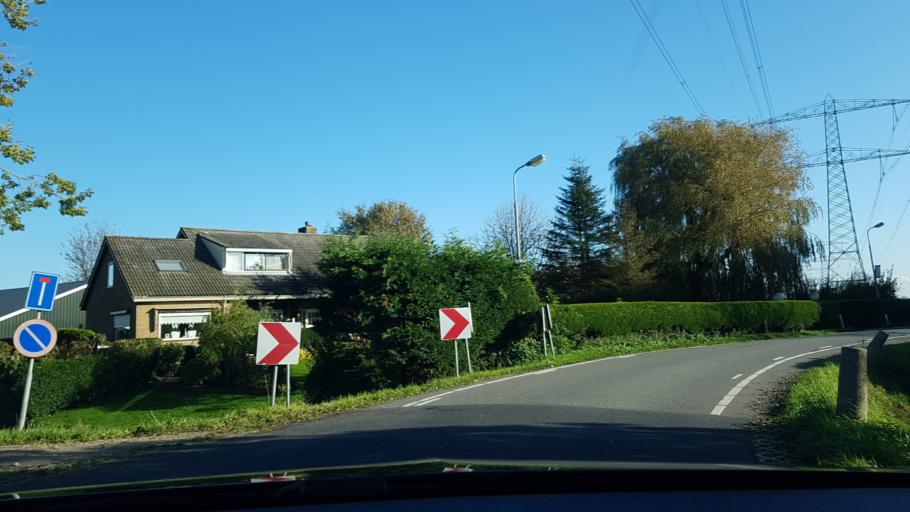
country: NL
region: North Holland
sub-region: Gemeente Beverwijk
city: Beverwijk
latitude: 52.4686
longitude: 4.6950
